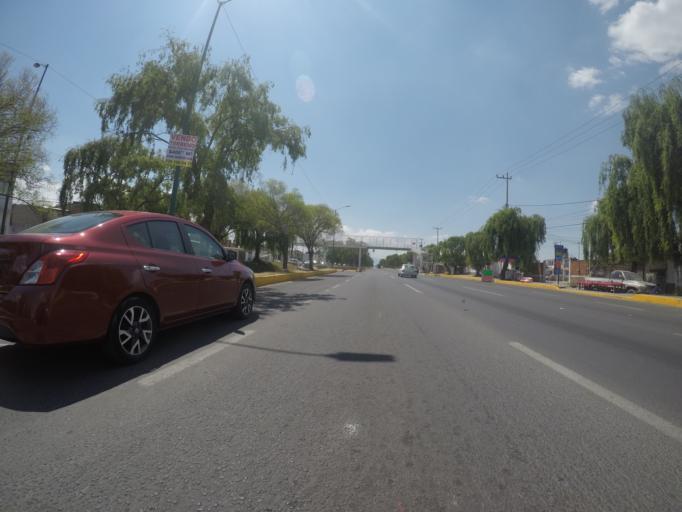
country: MX
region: Mexico
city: San Buenaventura
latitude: 19.2566
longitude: -99.6702
